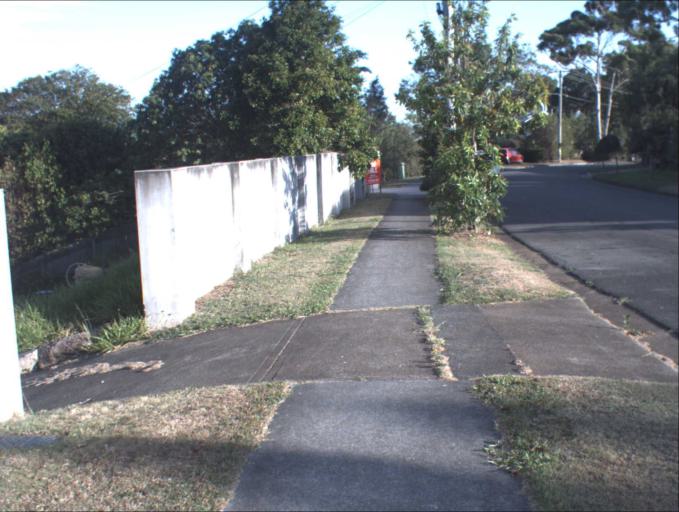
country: AU
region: Queensland
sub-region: Logan
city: Beenleigh
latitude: -27.6748
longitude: 153.2033
